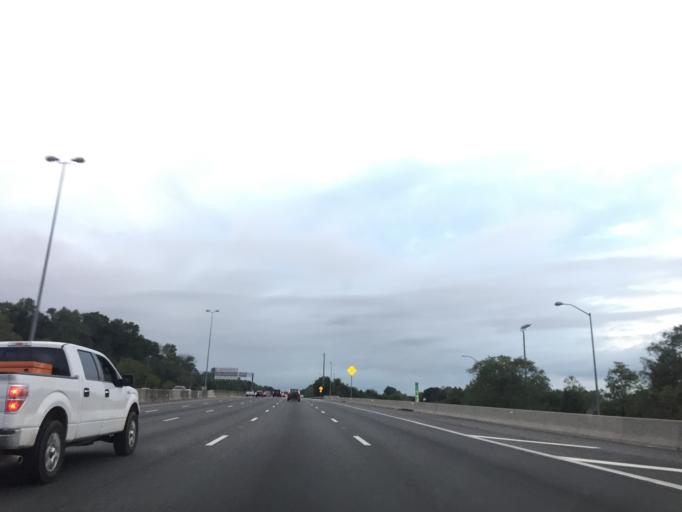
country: US
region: Virginia
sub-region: Fairfax County
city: Rose Hill
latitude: 38.8023
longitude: -77.1104
